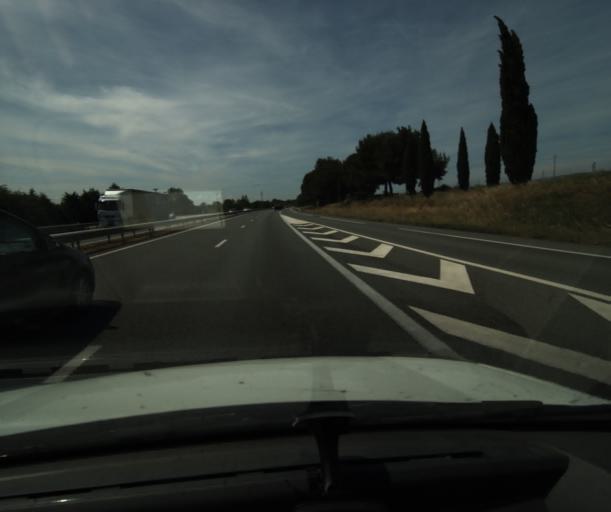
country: FR
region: Languedoc-Roussillon
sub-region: Departement de l'Aude
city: Bram
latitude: 43.2298
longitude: 2.1125
